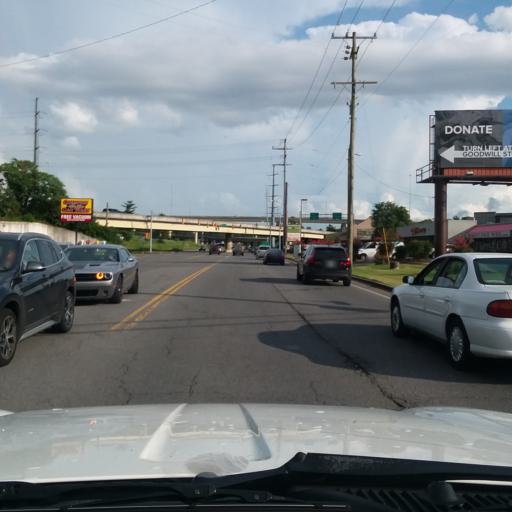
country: US
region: Tennessee
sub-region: Davidson County
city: Oak Hill
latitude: 36.1200
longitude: -86.7750
